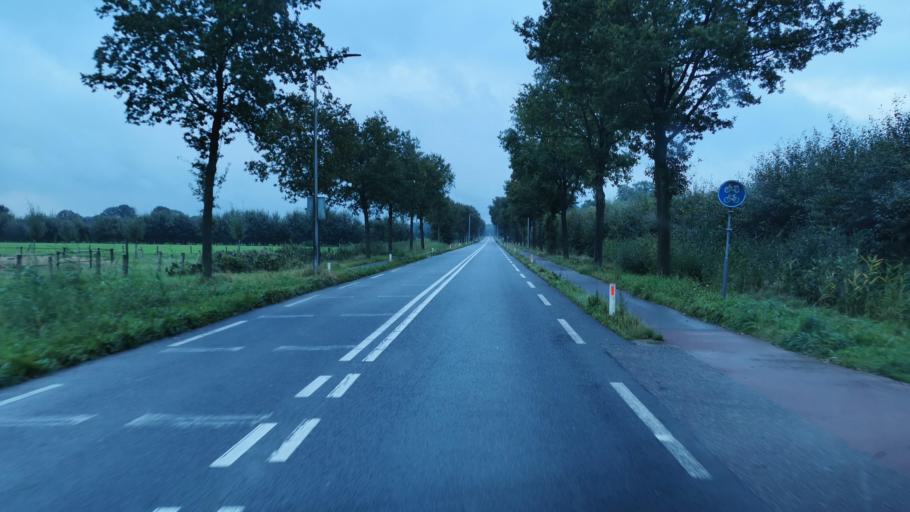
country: NL
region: Overijssel
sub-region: Gemeente Enschede
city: Enschede
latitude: 52.1877
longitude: 6.9057
